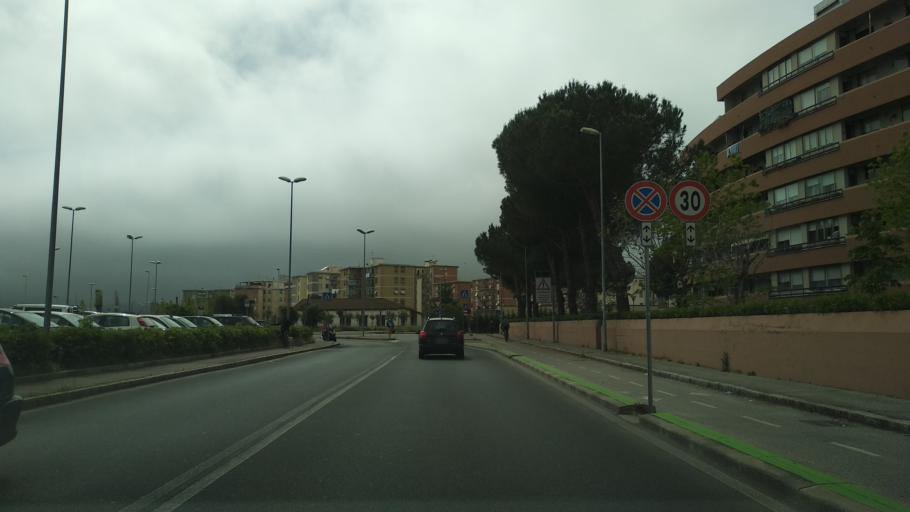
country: IT
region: Tuscany
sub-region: Provincia di Livorno
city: Livorno
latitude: 43.5408
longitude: 10.3302
